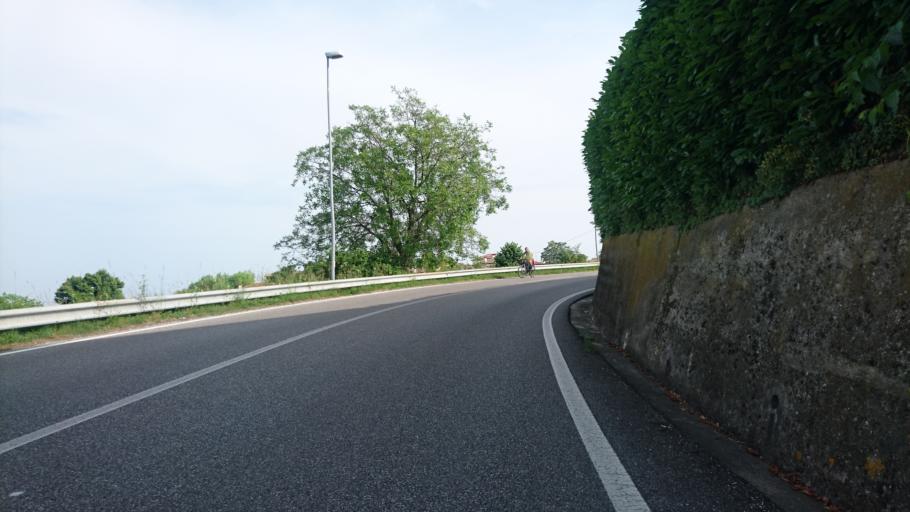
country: IT
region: Veneto
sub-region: Provincia di Treviso
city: Carpesica
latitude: 45.9528
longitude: 12.2921
